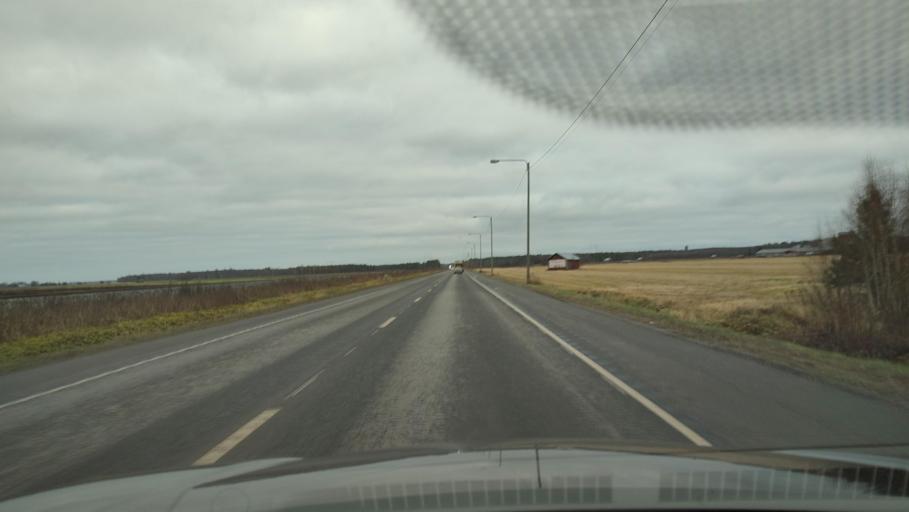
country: FI
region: Southern Ostrobothnia
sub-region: Seinaejoki
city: Ilmajoki
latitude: 62.7390
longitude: 22.6146
